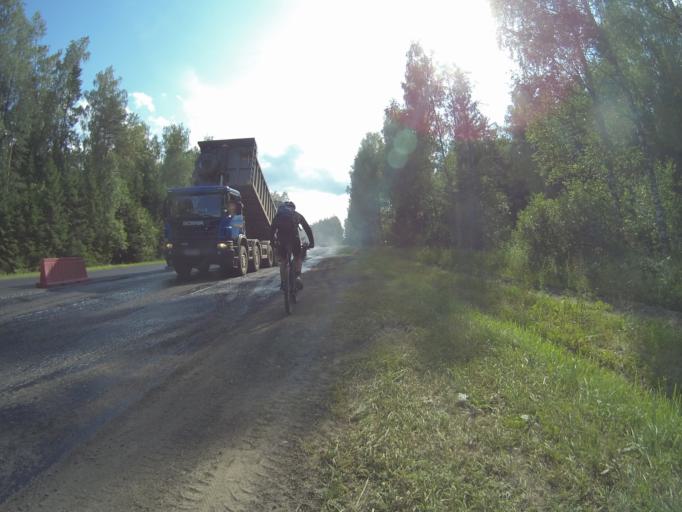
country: RU
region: Ivanovo
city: Novoye Leushino
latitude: 56.7094
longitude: 40.6495
